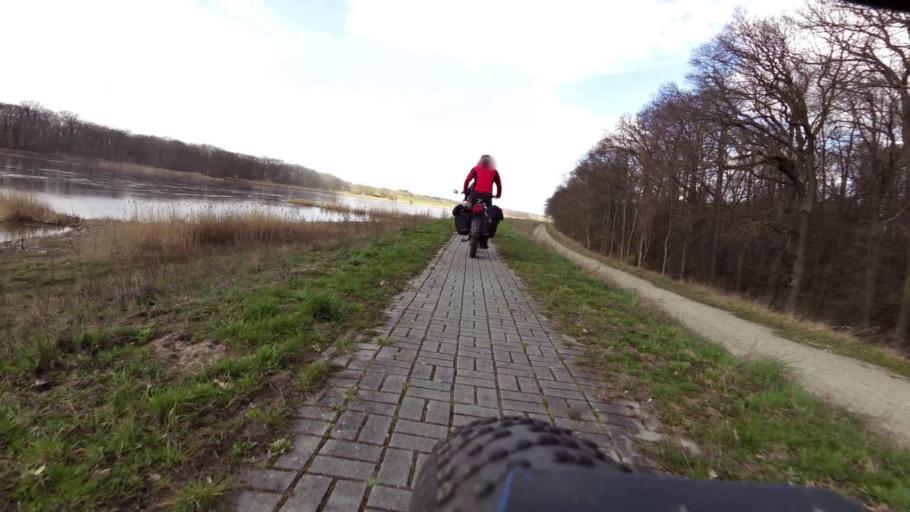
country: PL
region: Lubusz
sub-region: Powiat slubicki
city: Slubice
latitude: 52.3872
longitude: 14.5432
